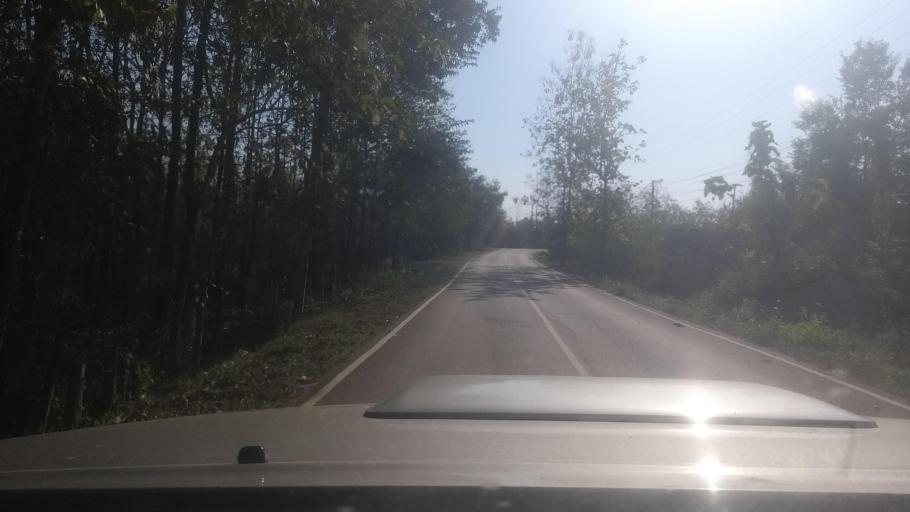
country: TH
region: Phrae
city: Phrae
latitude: 18.2527
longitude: 99.9934
